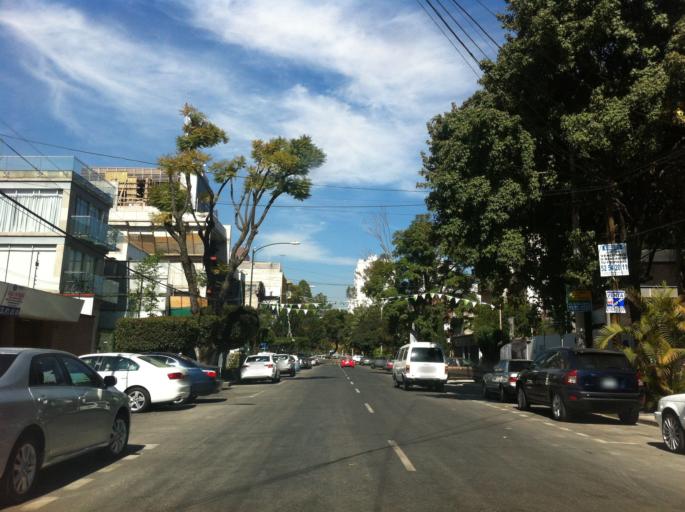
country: MX
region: Mexico City
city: Miguel Hidalgo
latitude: 19.4365
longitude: -99.1931
